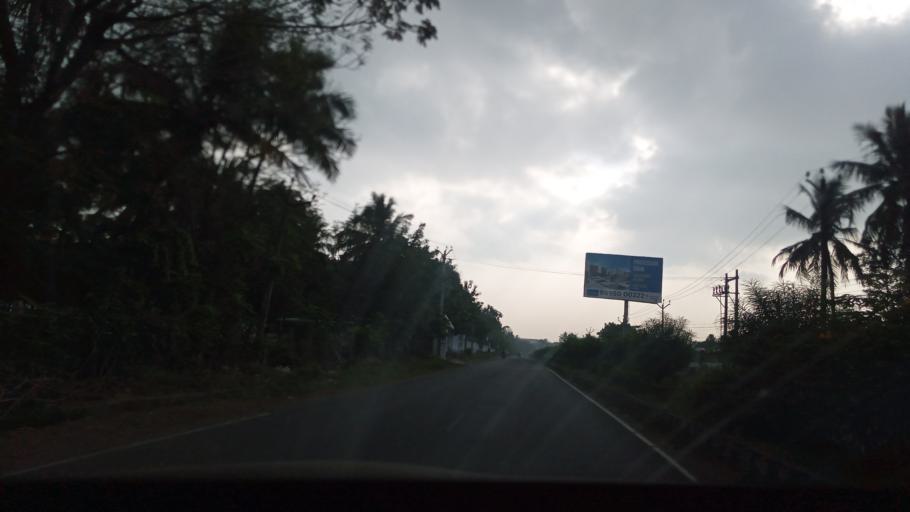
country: IN
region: Tamil Nadu
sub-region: Kancheepuram
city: Vengavasal
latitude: 12.7932
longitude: 80.2129
